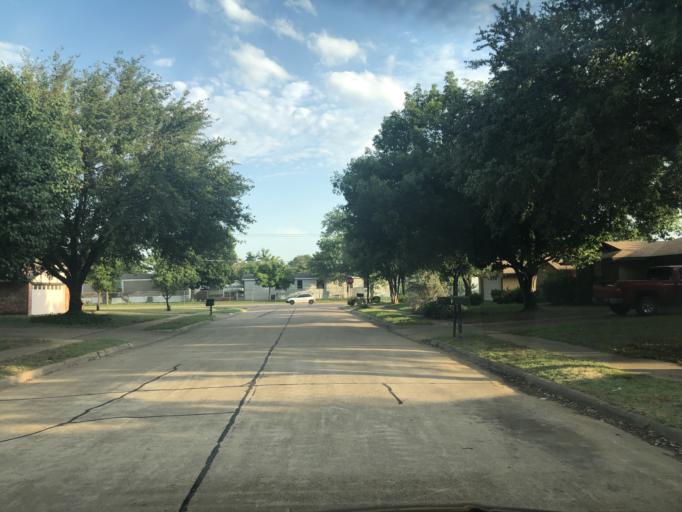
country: US
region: Texas
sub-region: Dallas County
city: Irving
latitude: 32.7946
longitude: -96.9548
